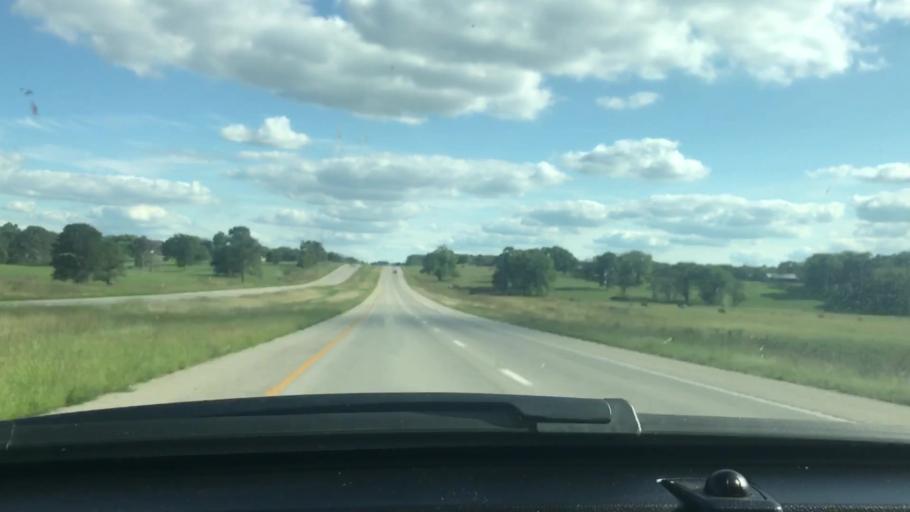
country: US
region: Missouri
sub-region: Howell County
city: West Plains
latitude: 36.8414
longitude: -91.9187
